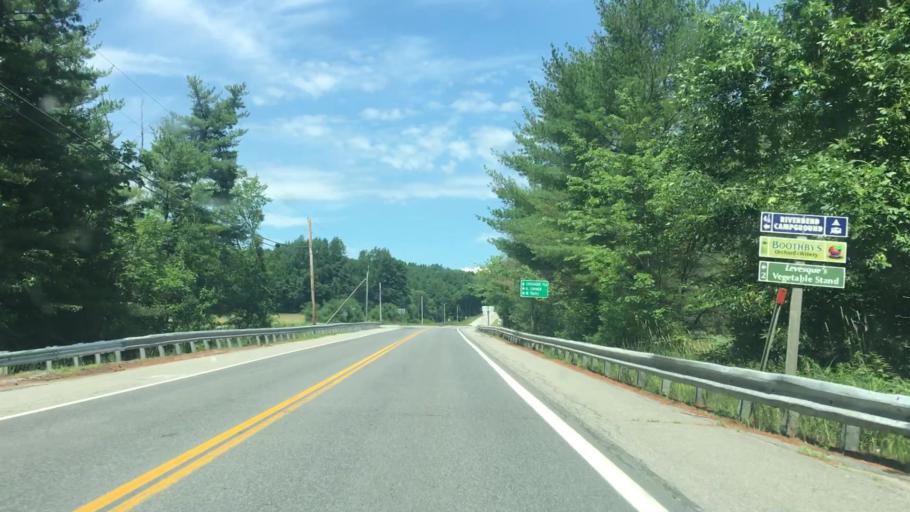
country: US
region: Maine
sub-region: Kennebec County
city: Wayne
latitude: 44.3570
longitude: -70.0807
